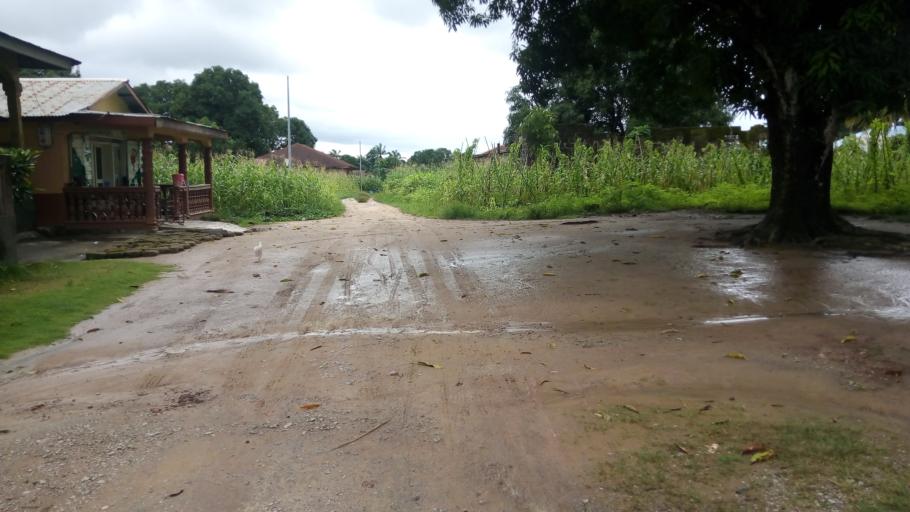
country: SL
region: Northern Province
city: Lunsar
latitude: 8.6912
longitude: -12.5357
